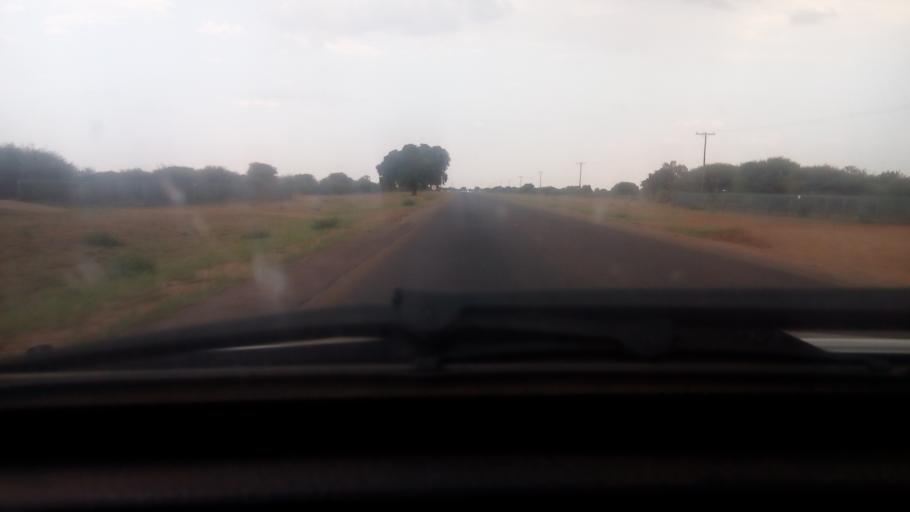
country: BW
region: Kweneng
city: Metsemotlhaba
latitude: -24.4738
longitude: 25.7071
